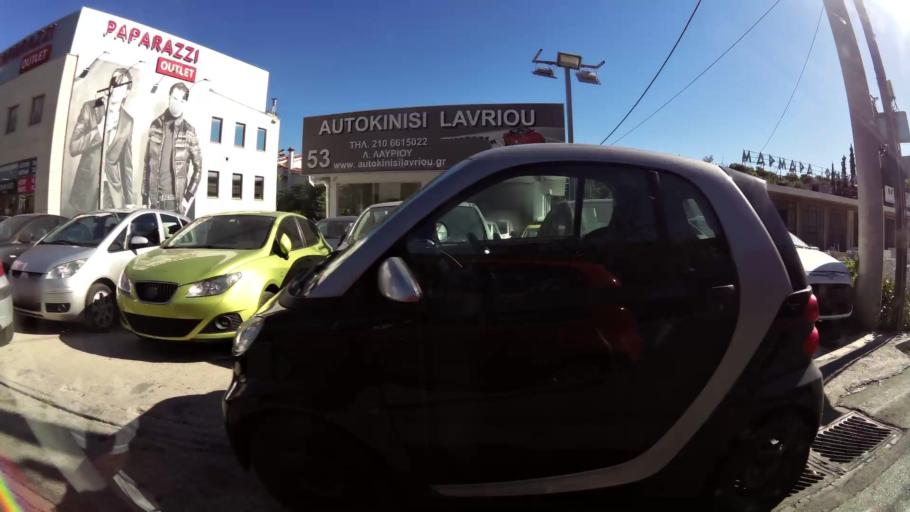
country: GR
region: Attica
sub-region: Nomarchia Athinas
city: Agia Paraskevi
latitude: 38.0045
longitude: 23.8474
